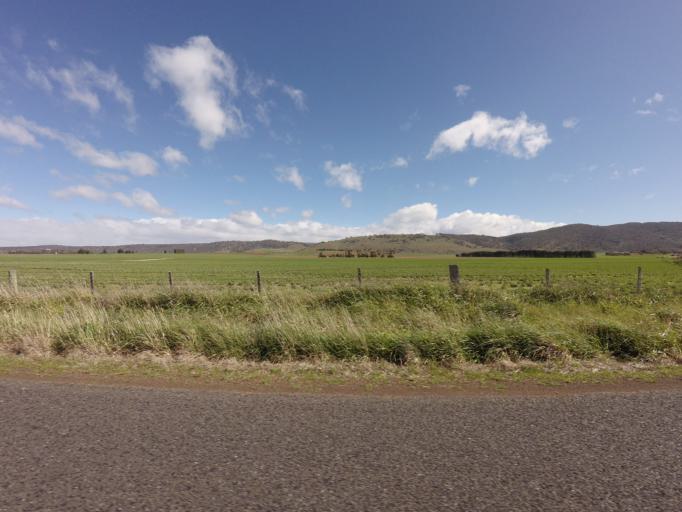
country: AU
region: Tasmania
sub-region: Northern Midlands
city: Evandale
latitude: -42.0092
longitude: 147.4589
